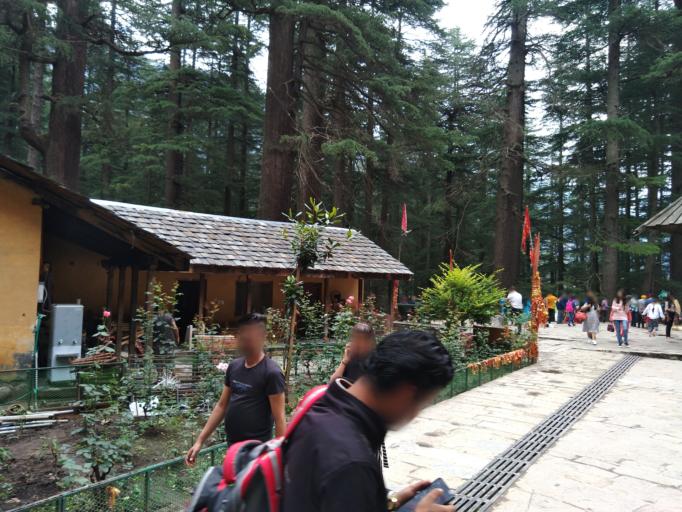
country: IN
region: Himachal Pradesh
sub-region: Kulu
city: Manali
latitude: 32.2485
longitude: 77.1806
